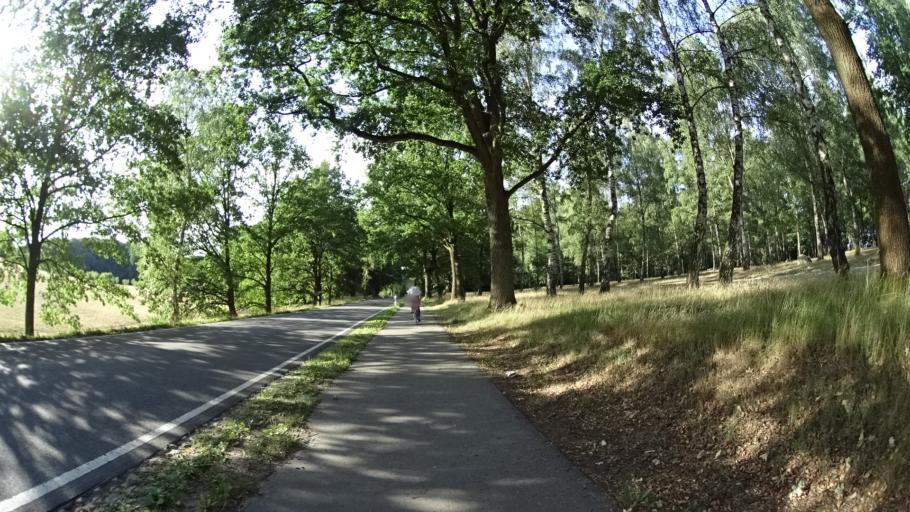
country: DE
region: Lower Saxony
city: Undeloh
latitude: 53.1510
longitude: 9.9077
